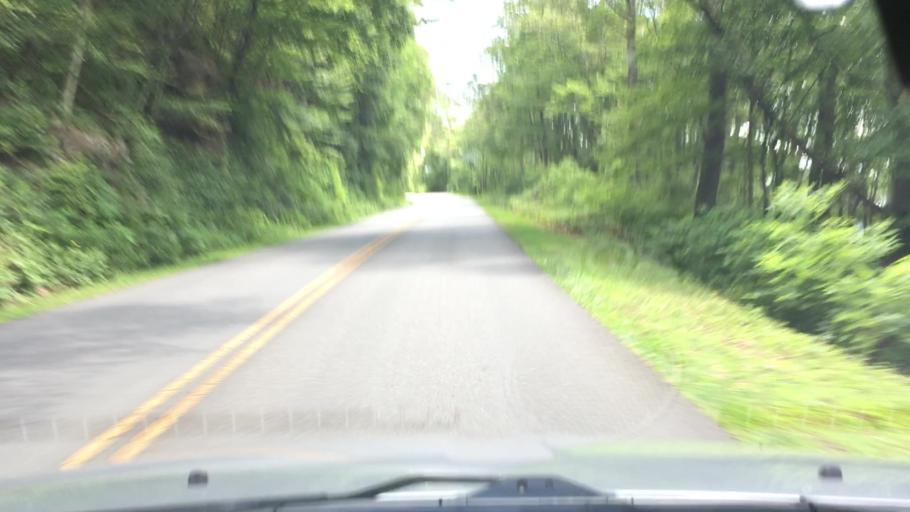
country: US
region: North Carolina
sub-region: Buncombe County
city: Swannanoa
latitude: 35.6760
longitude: -82.4394
